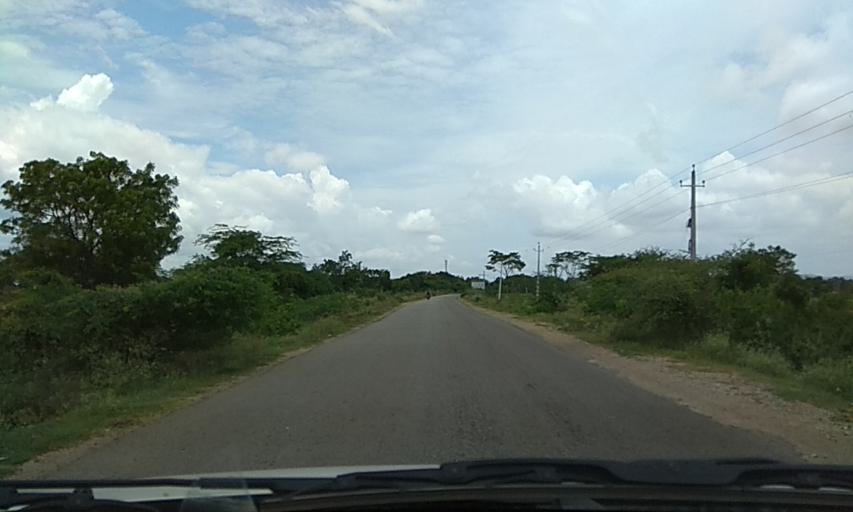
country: IN
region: Karnataka
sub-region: Chamrajnagar
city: Gundlupet
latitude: 11.8116
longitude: 76.7433
